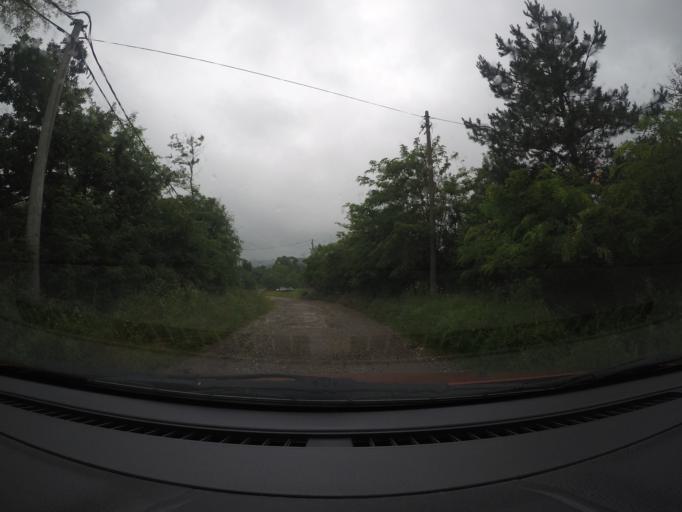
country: RS
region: Central Serbia
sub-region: Belgrade
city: Sopot
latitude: 44.5566
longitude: 20.5165
